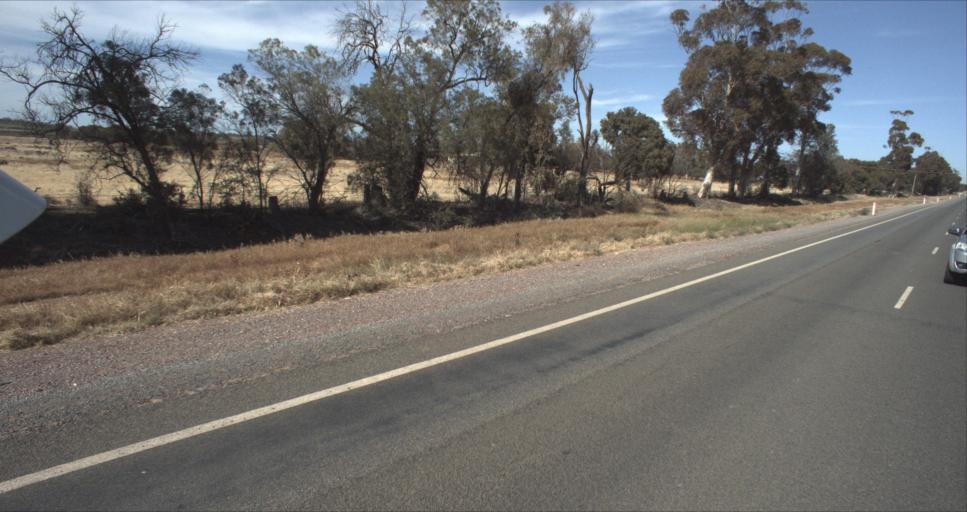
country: AU
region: New South Wales
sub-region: Leeton
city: Leeton
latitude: -34.5601
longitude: 146.4389
